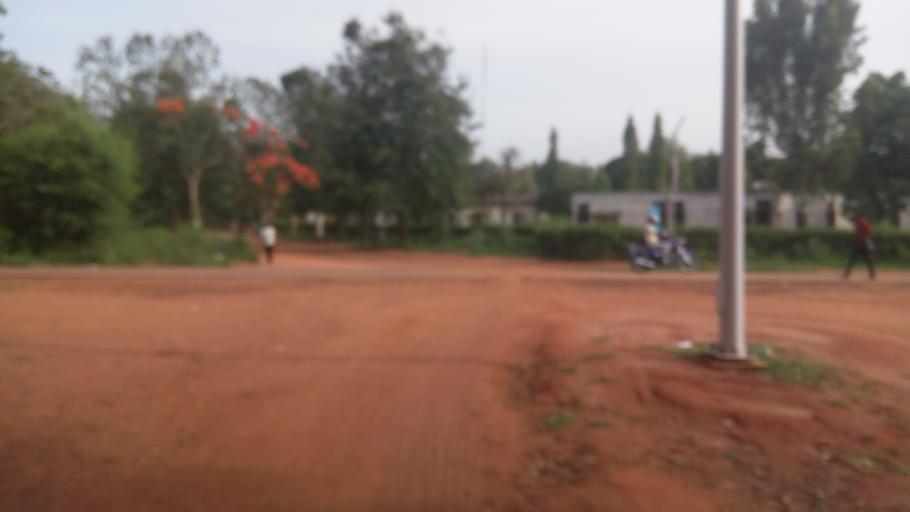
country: TG
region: Maritime
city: Lome
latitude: 6.1701
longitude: 1.2143
